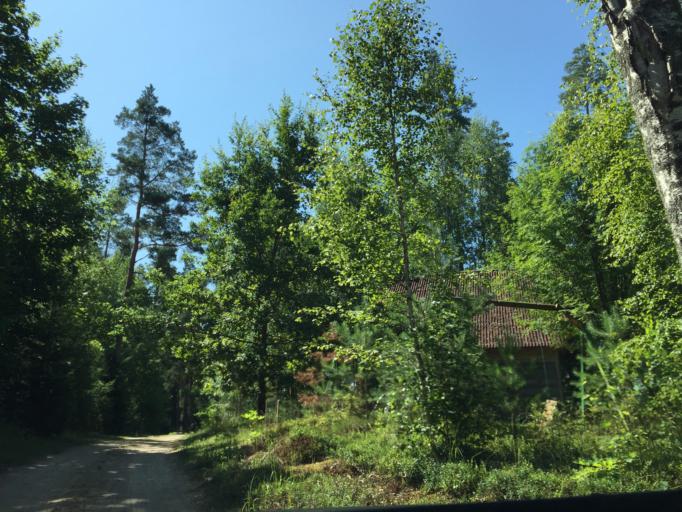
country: LV
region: Talsu Rajons
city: Stende
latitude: 57.1609
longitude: 22.3039
